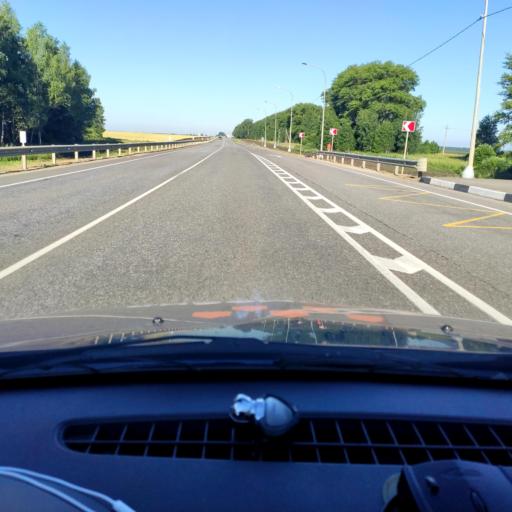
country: RU
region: Orjol
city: Pokrovskoye
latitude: 52.6419
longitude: 36.6663
